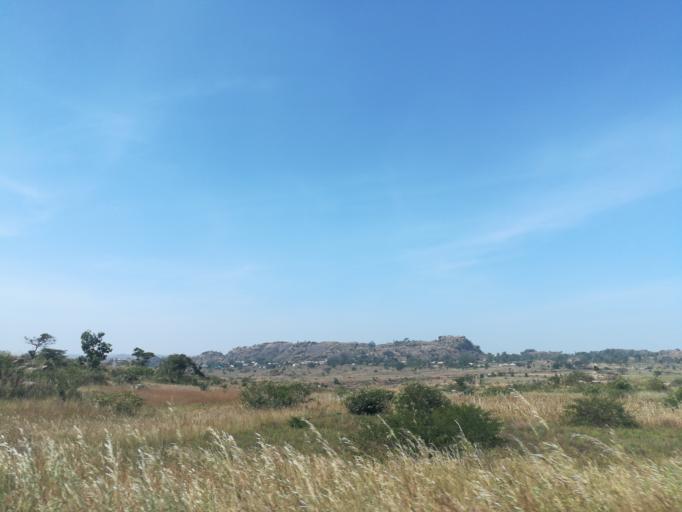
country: NG
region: Plateau
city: Bukuru
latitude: 9.7607
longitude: 8.9068
